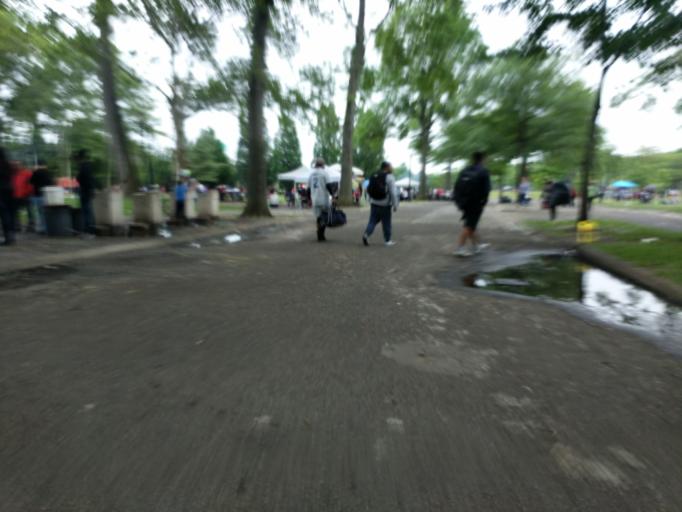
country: US
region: New York
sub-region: Queens County
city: Jamaica
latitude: 40.7475
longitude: -73.8363
